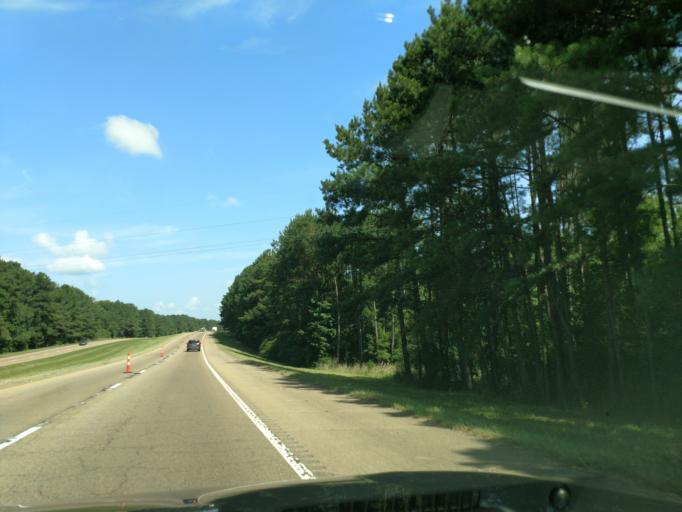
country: US
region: Mississippi
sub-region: Simpson County
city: Mendenhall
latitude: 31.9271
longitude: -89.8199
